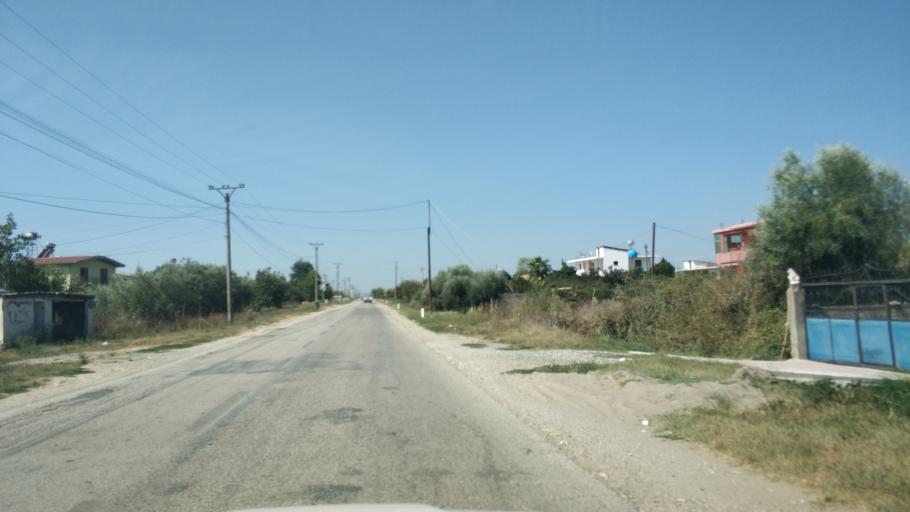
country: AL
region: Tirane
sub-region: Rrethi i Kavajes
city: Rrogozhine
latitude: 41.0519
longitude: 19.6461
